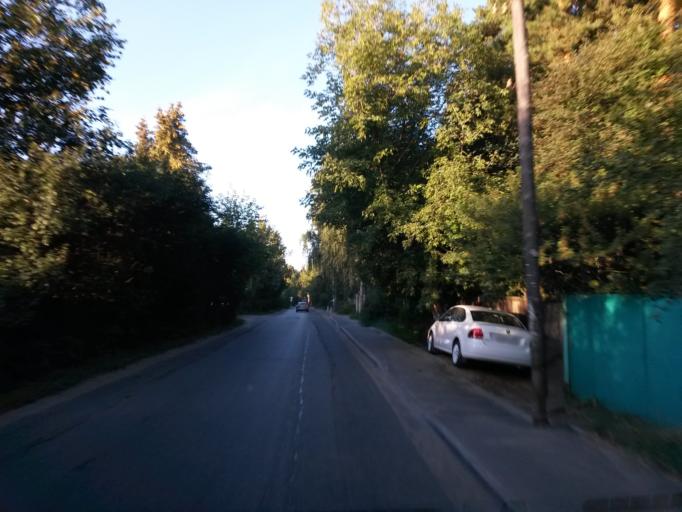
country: RU
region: Moskovskaya
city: Mamontovka
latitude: 55.9839
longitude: 37.8449
